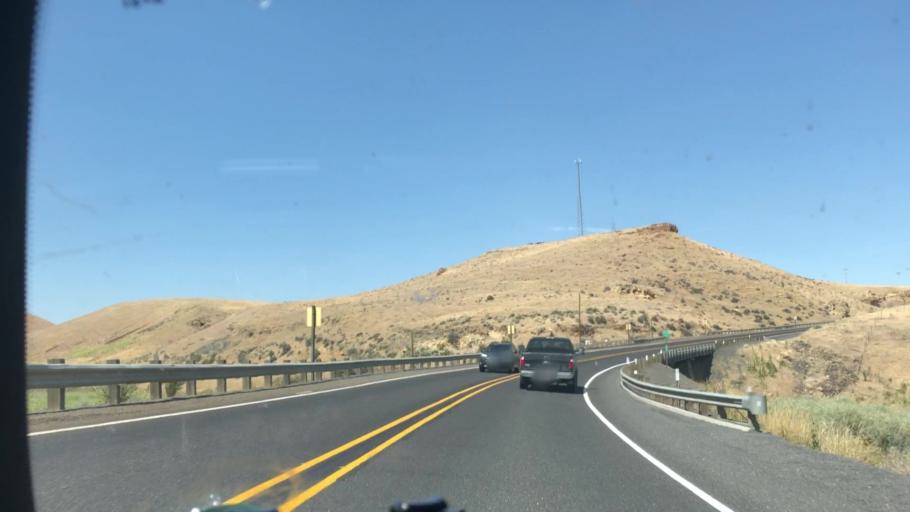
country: US
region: Idaho
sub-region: Owyhee County
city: Marsing
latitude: 43.2278
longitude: -117.0541
